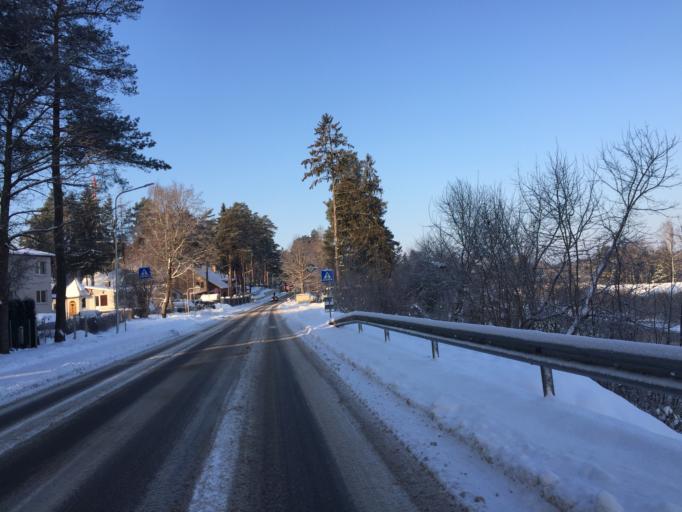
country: LV
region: Ogre
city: Ogre
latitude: 56.8077
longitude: 24.6293
